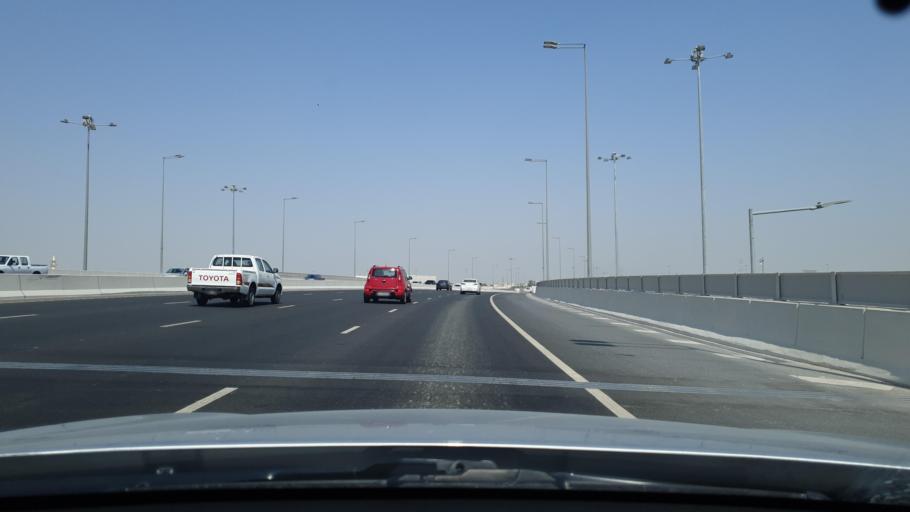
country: QA
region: Baladiyat ar Rayyan
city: Ar Rayyan
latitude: 25.3169
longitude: 51.4362
